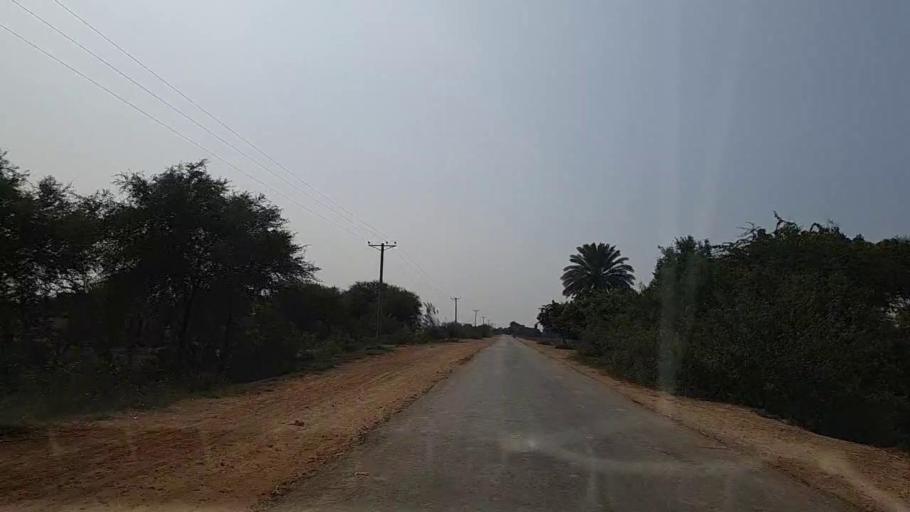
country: PK
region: Sindh
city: Chuhar Jamali
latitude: 24.3519
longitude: 67.9542
